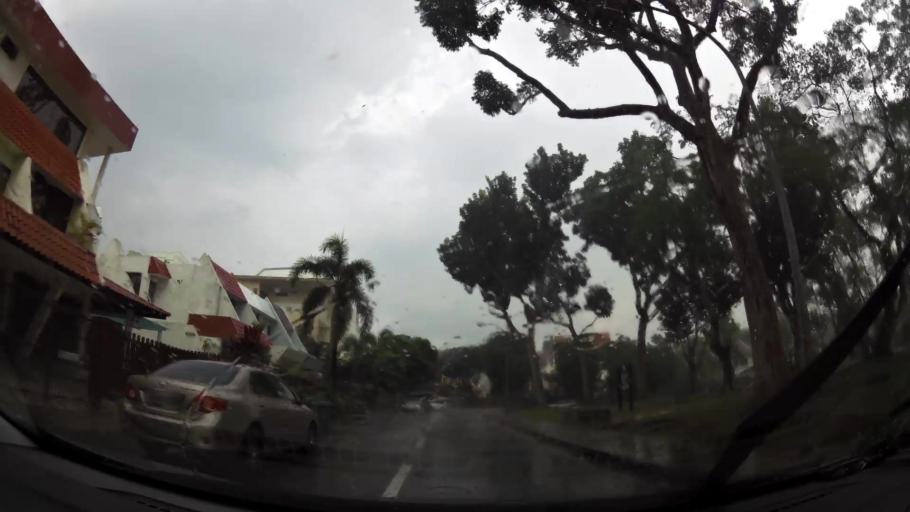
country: SG
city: Singapore
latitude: 1.3394
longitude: 103.9580
